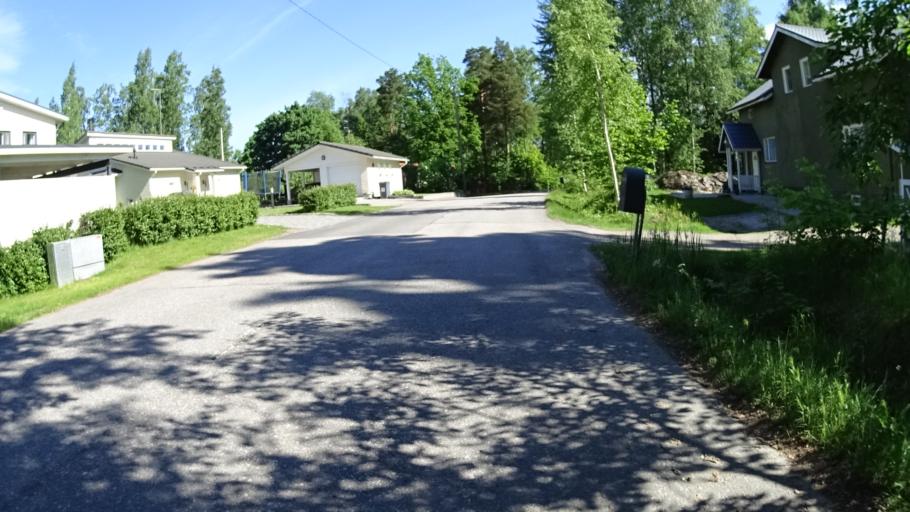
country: FI
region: Uusimaa
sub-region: Helsinki
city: Kilo
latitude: 60.2574
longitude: 24.7759
